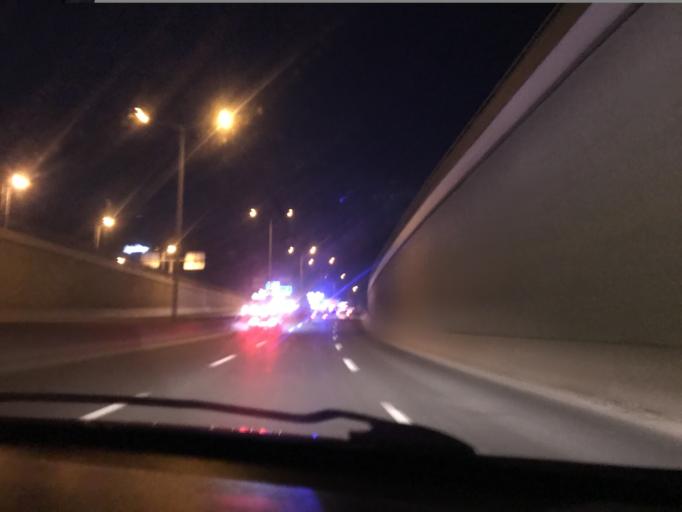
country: TR
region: Ankara
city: Batikent
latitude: 39.9458
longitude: 32.7114
